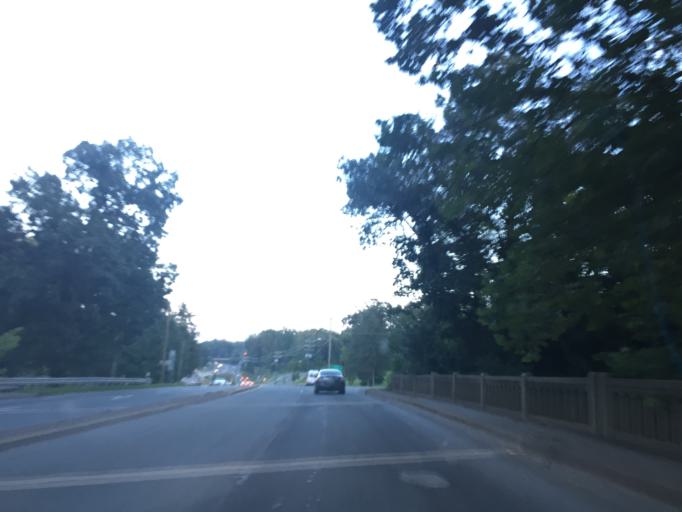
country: US
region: Virginia
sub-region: City of Charlottesville
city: Charlottesville
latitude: 38.0452
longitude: -78.4786
